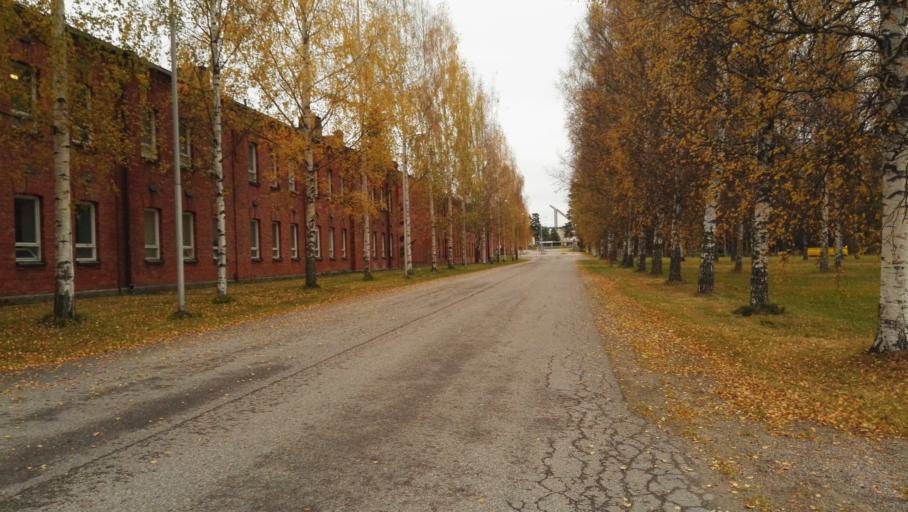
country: FI
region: Paijanne Tavastia
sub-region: Lahti
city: Lahti
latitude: 60.9679
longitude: 25.6237
